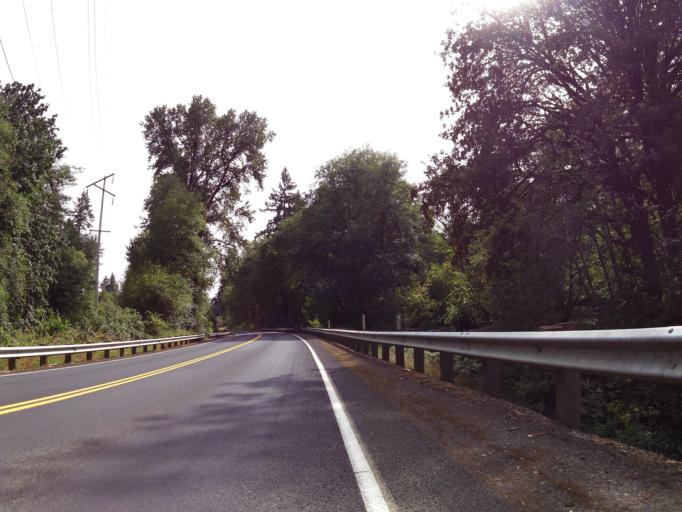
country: US
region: Washington
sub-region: Cowlitz County
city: Castle Rock
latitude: 46.3468
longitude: -122.9403
